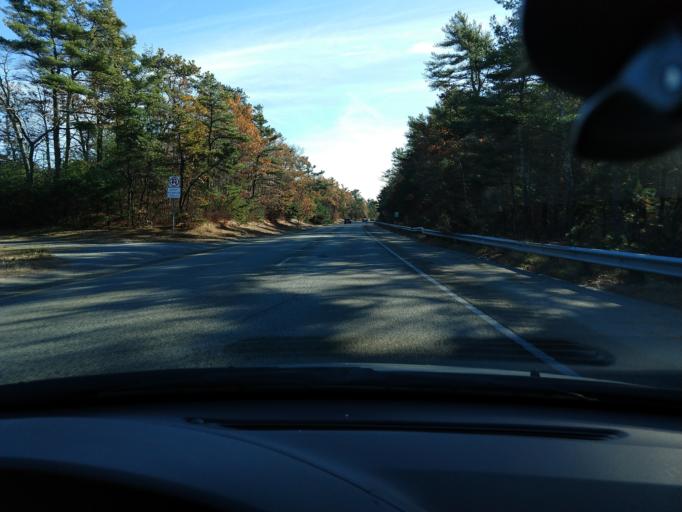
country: US
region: Massachusetts
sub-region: Plymouth County
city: White Island Shores
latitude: 41.8549
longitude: -70.5813
